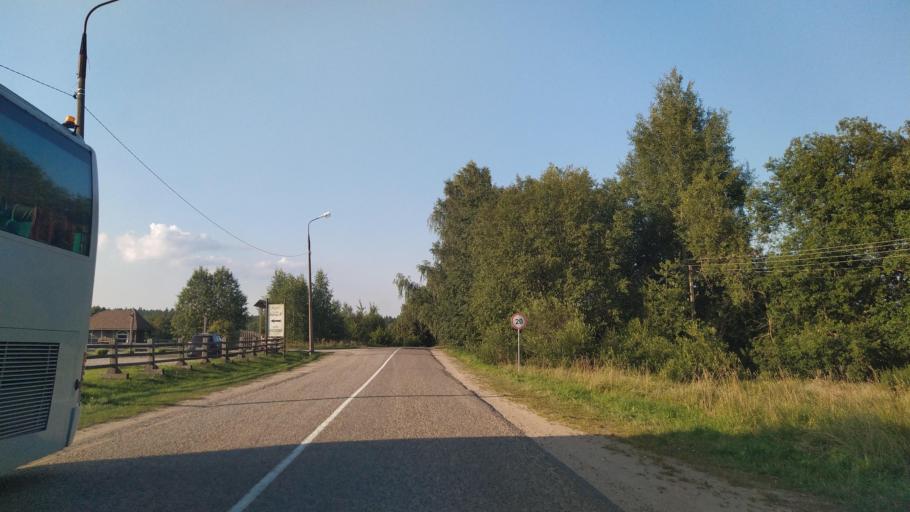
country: RU
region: Pskov
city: Pushkinskiye Gory
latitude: 57.0411
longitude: 28.9140
